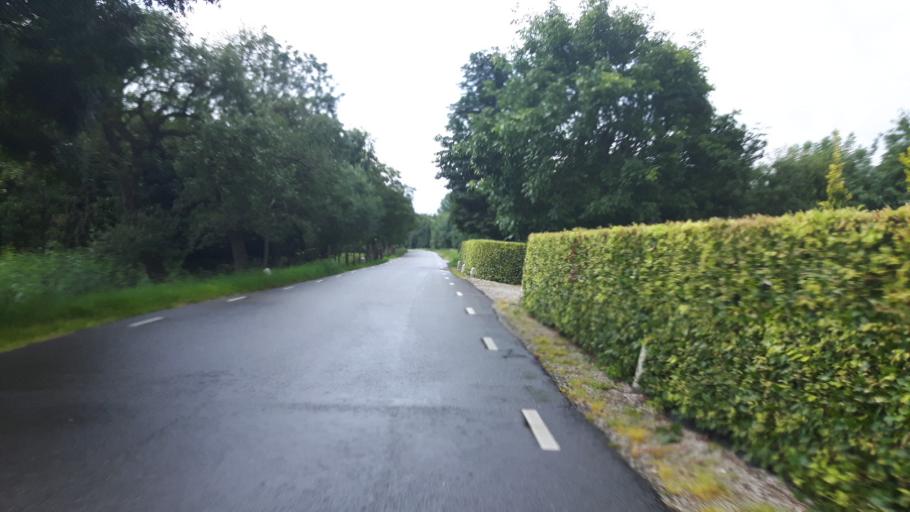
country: NL
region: Utrecht
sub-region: Gemeente Montfoort
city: Montfoort
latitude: 52.0348
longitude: 4.9294
